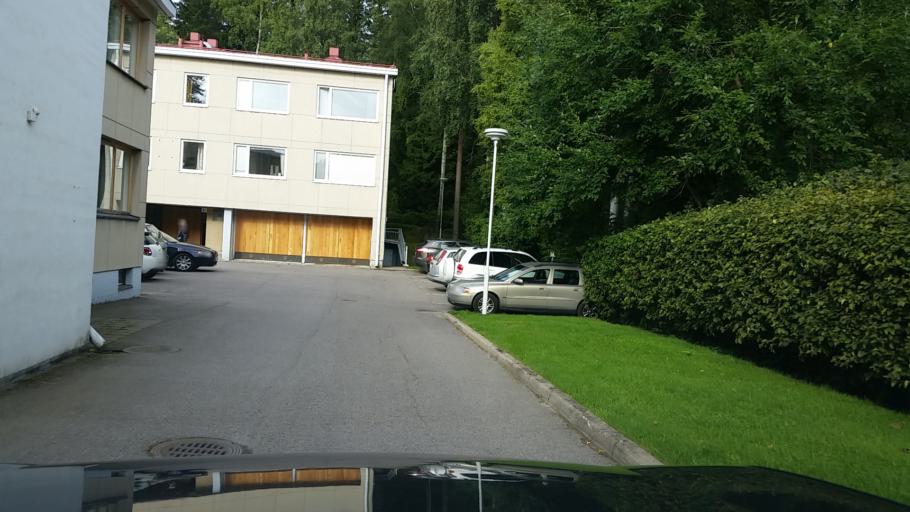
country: FI
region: Uusimaa
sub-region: Helsinki
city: Teekkarikylae
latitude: 60.1597
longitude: 24.8694
